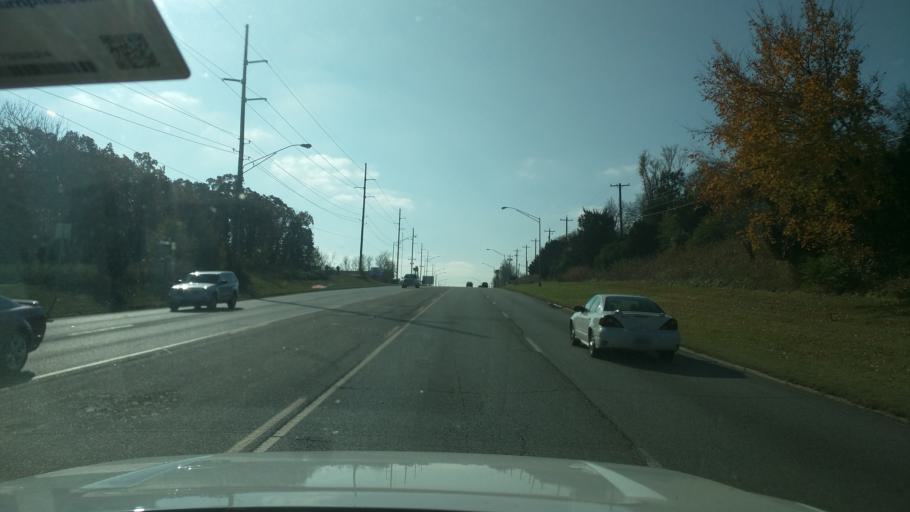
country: US
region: Oklahoma
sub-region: Washington County
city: Bartlesville
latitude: 36.7391
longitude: -95.9353
